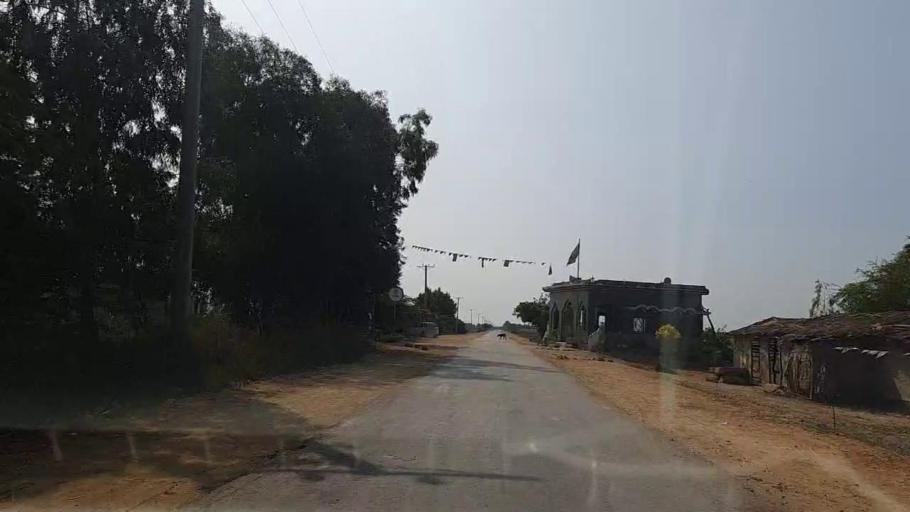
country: PK
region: Sindh
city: Chuhar Jamali
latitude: 24.3582
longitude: 67.9585
